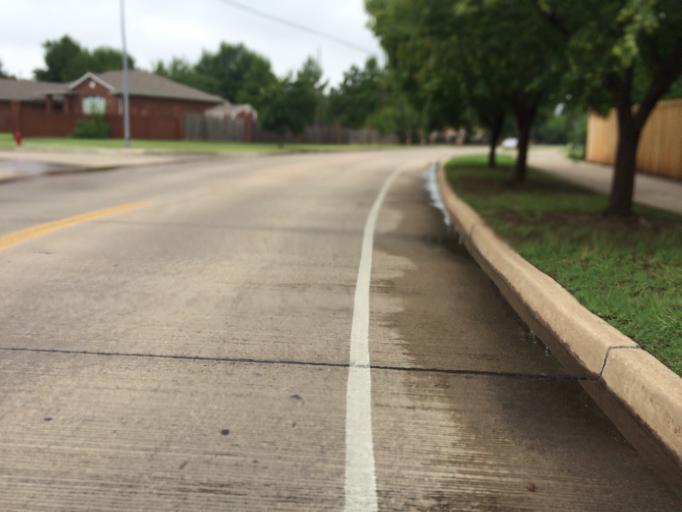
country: US
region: Oklahoma
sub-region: Cleveland County
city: Norman
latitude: 35.2113
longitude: -97.4251
